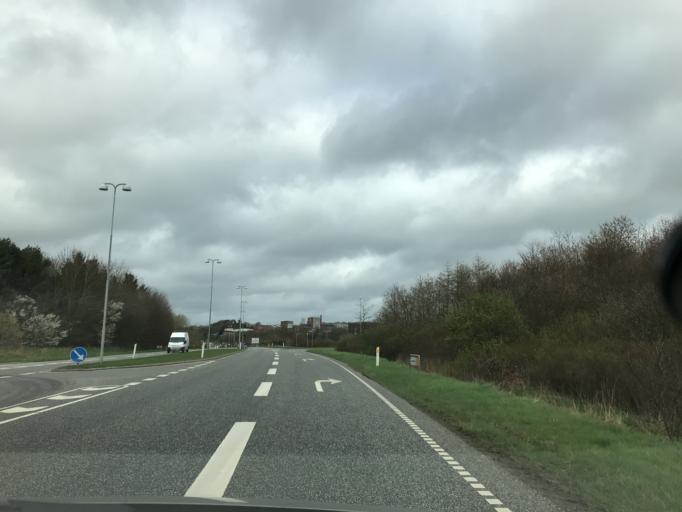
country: DK
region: Central Jutland
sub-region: Skive Kommune
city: Skive
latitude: 56.5789
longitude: 9.0227
